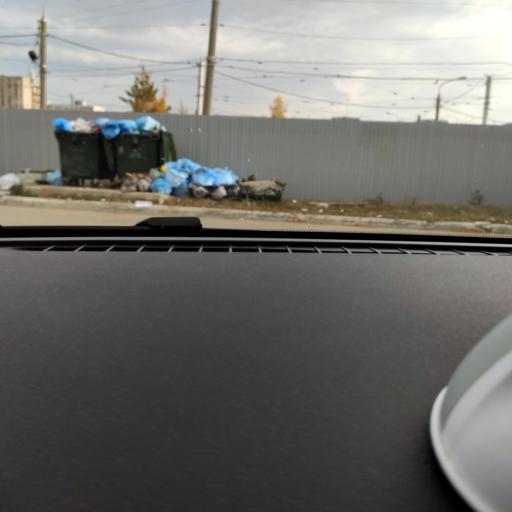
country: RU
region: Samara
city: Samara
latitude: 53.2325
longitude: 50.2058
